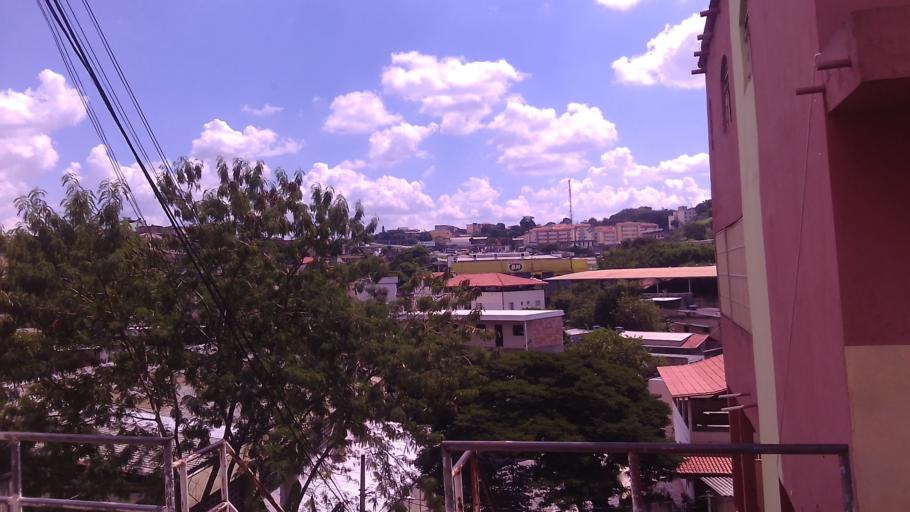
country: BR
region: Minas Gerais
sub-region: Belo Horizonte
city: Belo Horizonte
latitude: -19.8593
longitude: -43.9033
